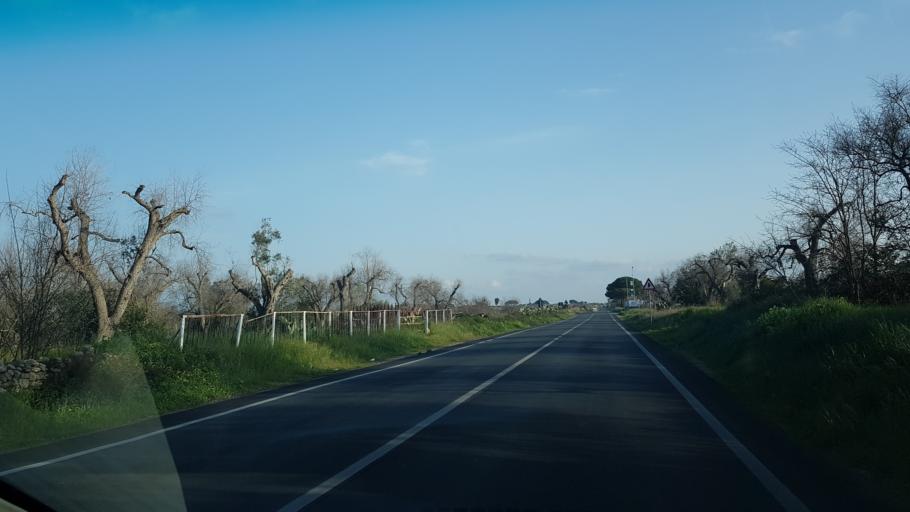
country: IT
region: Apulia
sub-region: Provincia di Lecce
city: Squinzano
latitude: 40.4253
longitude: 18.0549
